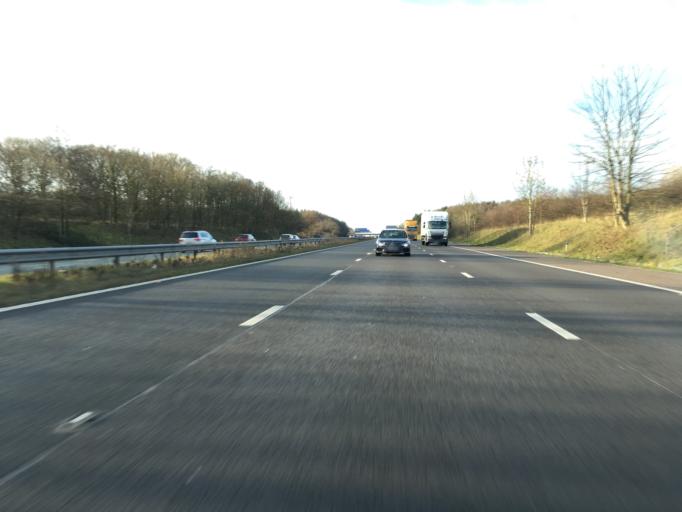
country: GB
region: England
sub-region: Warrington
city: Lymm
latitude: 53.3601
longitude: -2.4737
